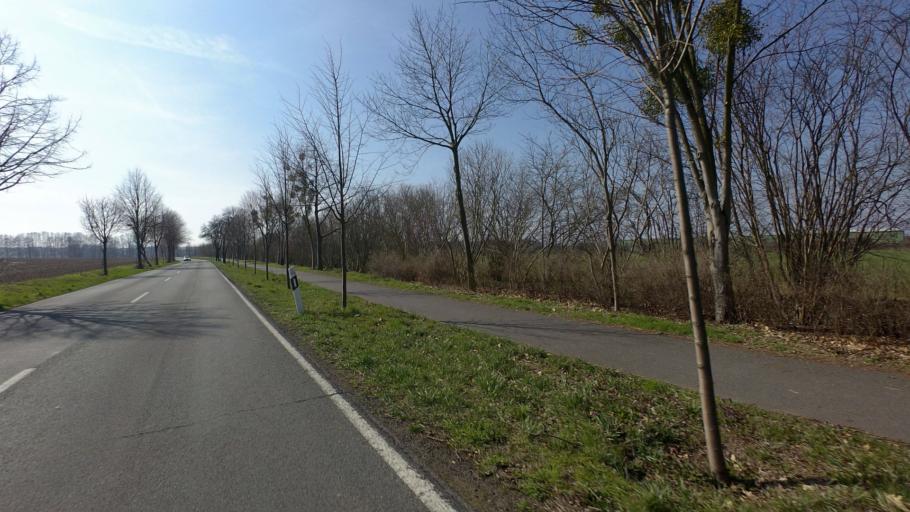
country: DE
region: Brandenburg
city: Golssen
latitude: 51.9677
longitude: 13.5991
